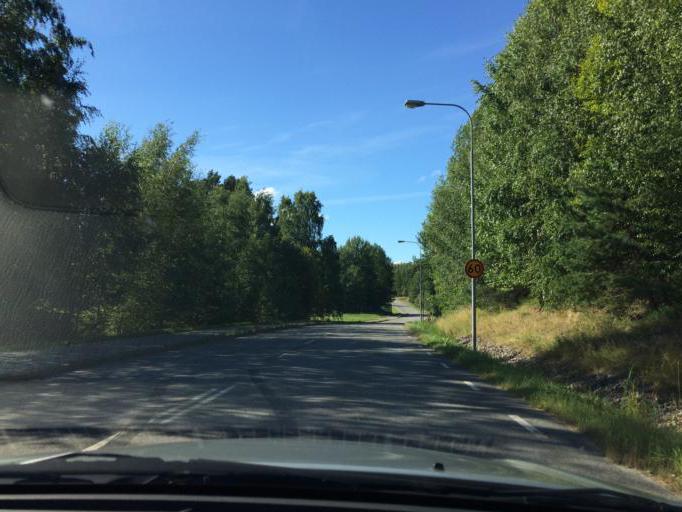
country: SE
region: Vaestmanland
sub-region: Vasteras
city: Vasteras
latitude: 59.6006
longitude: 16.6260
